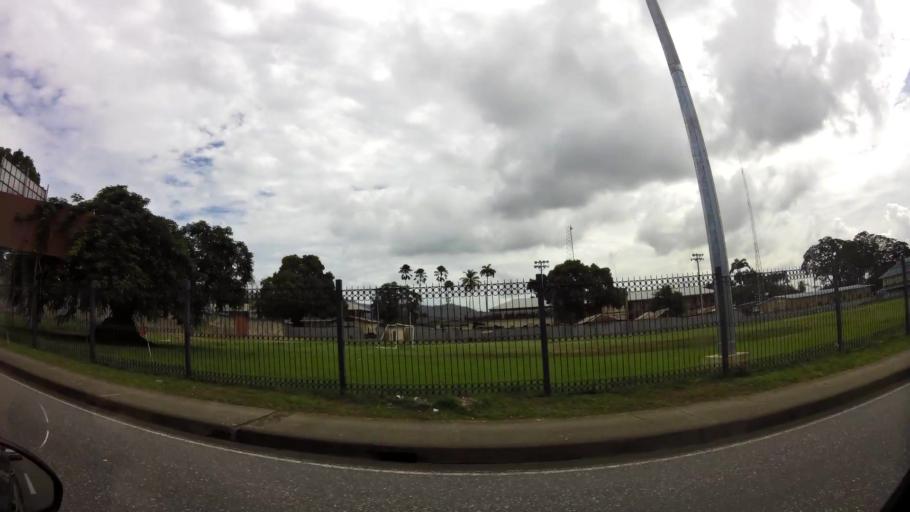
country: TT
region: City of Port of Spain
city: Port-of-Spain
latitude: 10.6724
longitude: -61.5294
